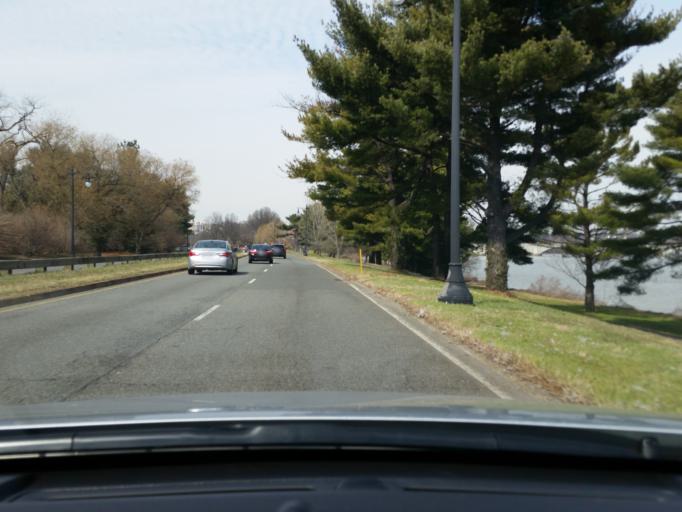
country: US
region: Washington, D.C.
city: Washington, D.C.
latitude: 38.8797
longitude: -77.0515
